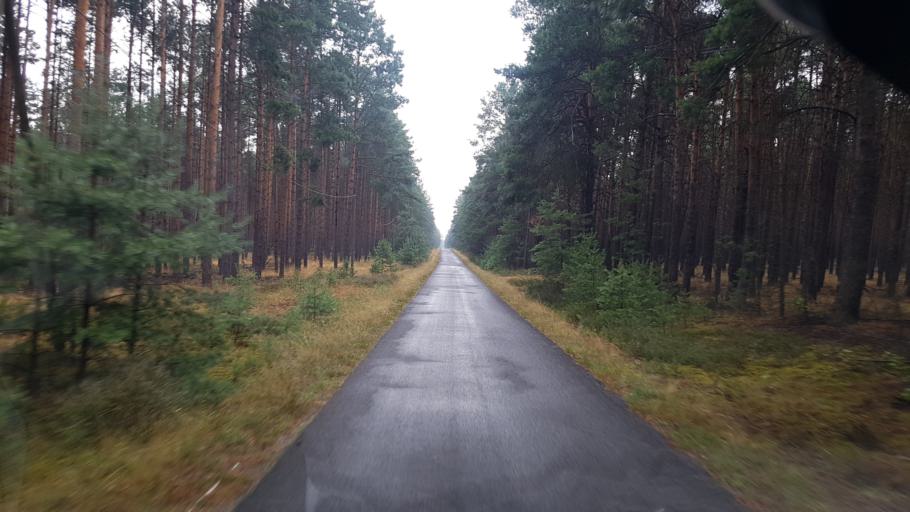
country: DE
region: Brandenburg
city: Finsterwalde
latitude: 51.6467
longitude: 13.7848
